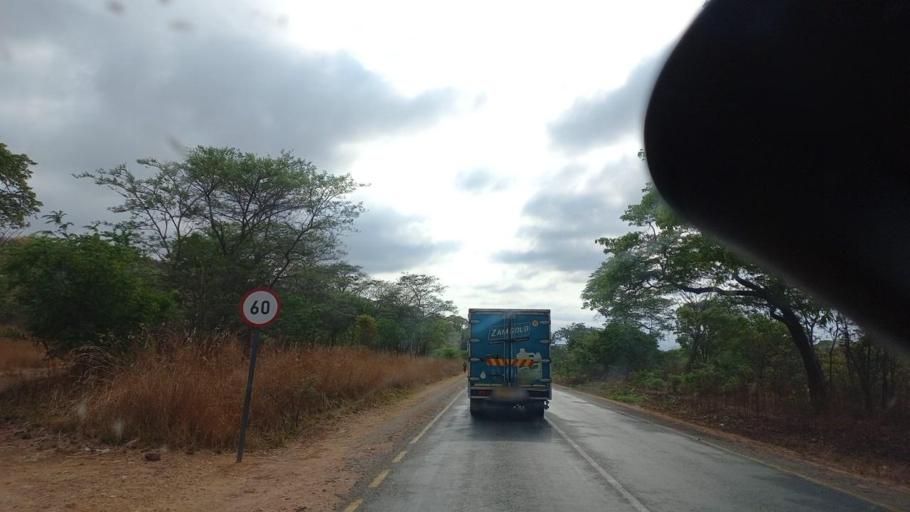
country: ZM
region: Lusaka
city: Chongwe
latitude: -15.2708
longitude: 28.8983
